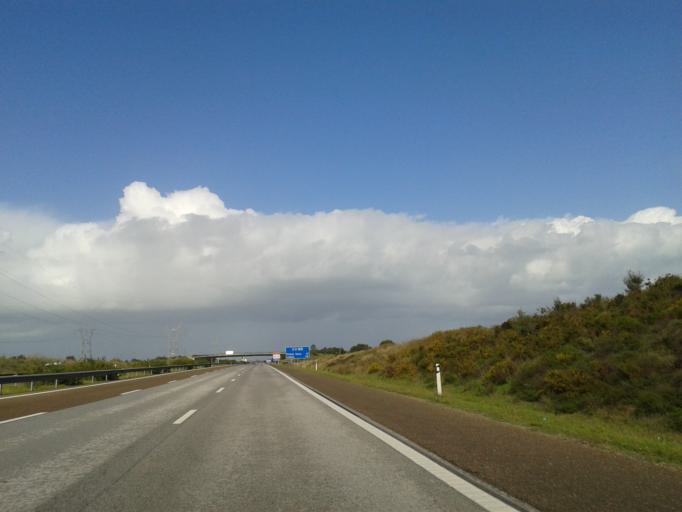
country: PT
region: Setubal
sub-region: Palmela
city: Palmela
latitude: 38.5945
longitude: -8.8653
